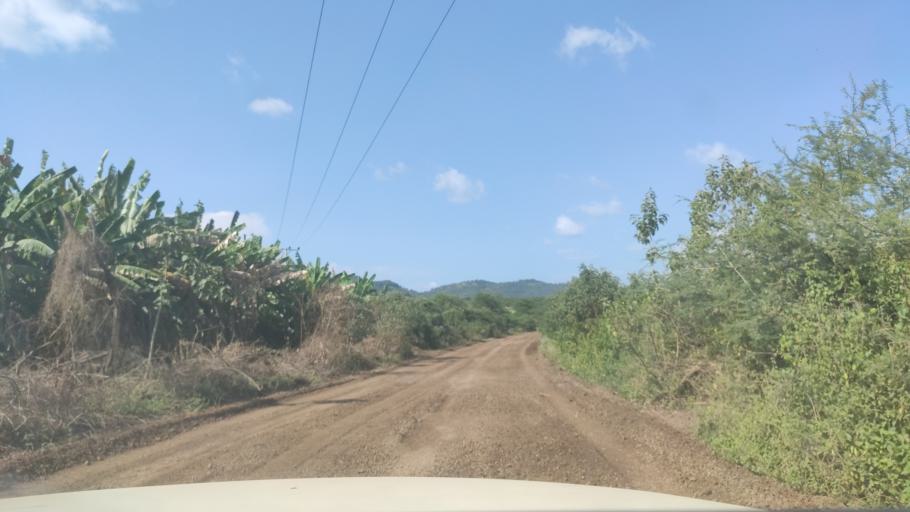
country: ET
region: Southern Nations, Nationalities, and People's Region
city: Felege Neway
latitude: 6.3758
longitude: 37.0876
